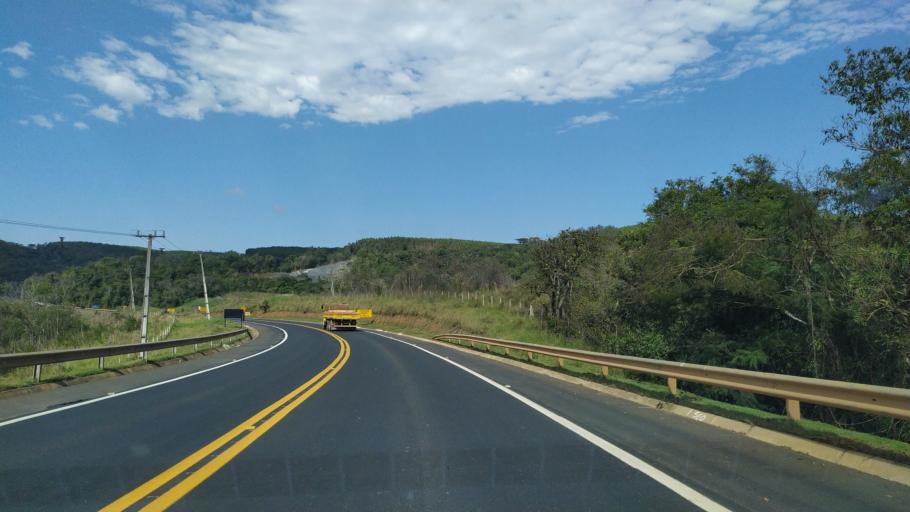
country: BR
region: Parana
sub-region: Telemaco Borba
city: Telemaco Borba
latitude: -24.2893
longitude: -50.7052
